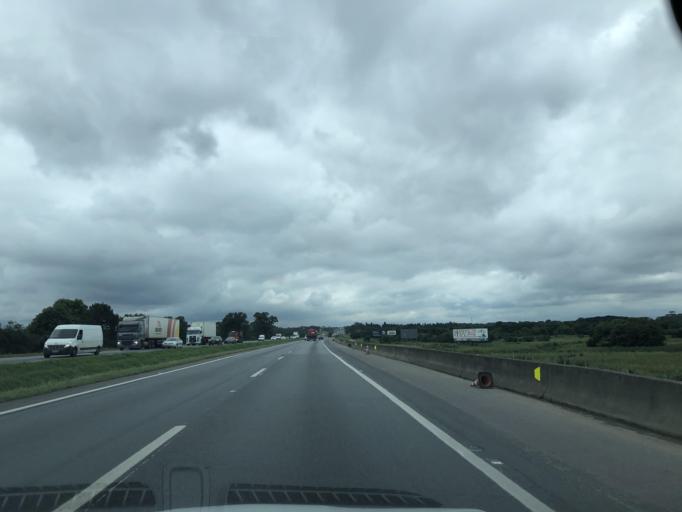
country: BR
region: Parana
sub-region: Sao Jose Dos Pinhais
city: Sao Jose dos Pinhais
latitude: -25.5681
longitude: -49.2331
